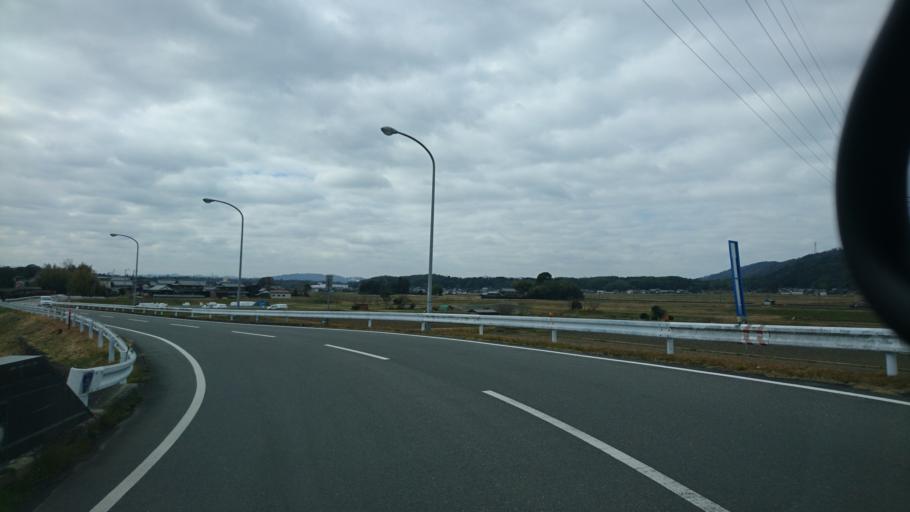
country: JP
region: Mie
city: Ueno-ebisumachi
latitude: 34.7512
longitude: 136.1157
